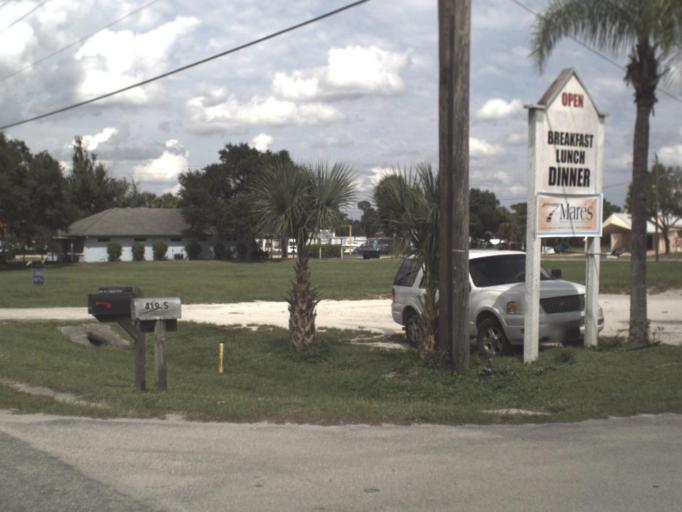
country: US
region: Florida
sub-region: Hendry County
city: LaBelle
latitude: 26.7555
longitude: -81.4382
